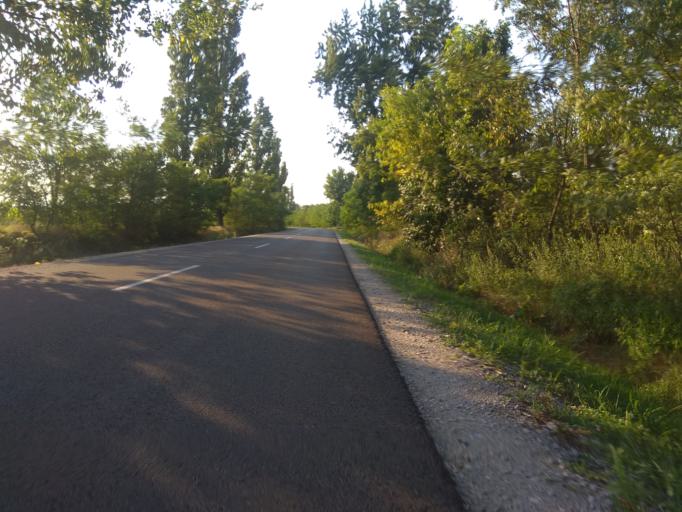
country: HU
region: Borsod-Abauj-Zemplen
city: Nyekladhaza
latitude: 47.9623
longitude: 20.8625
